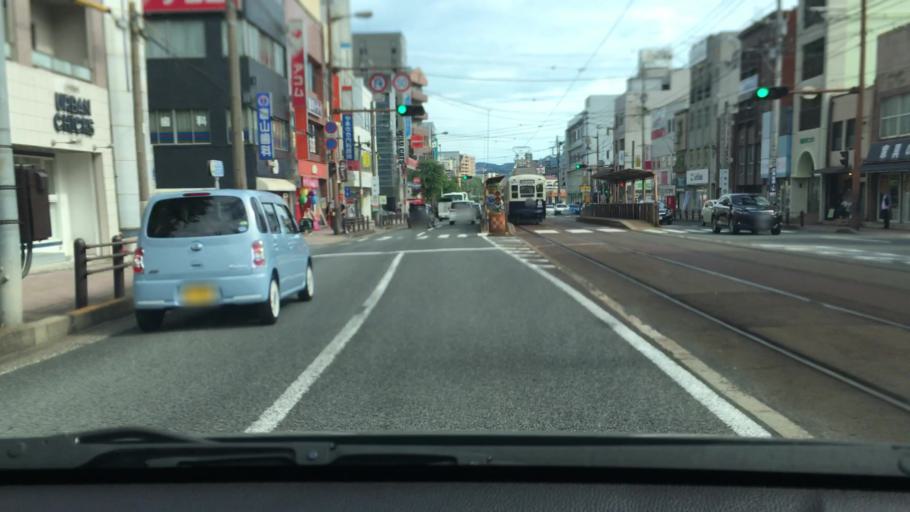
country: JP
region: Nagasaki
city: Obita
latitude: 32.7900
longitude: 129.8609
